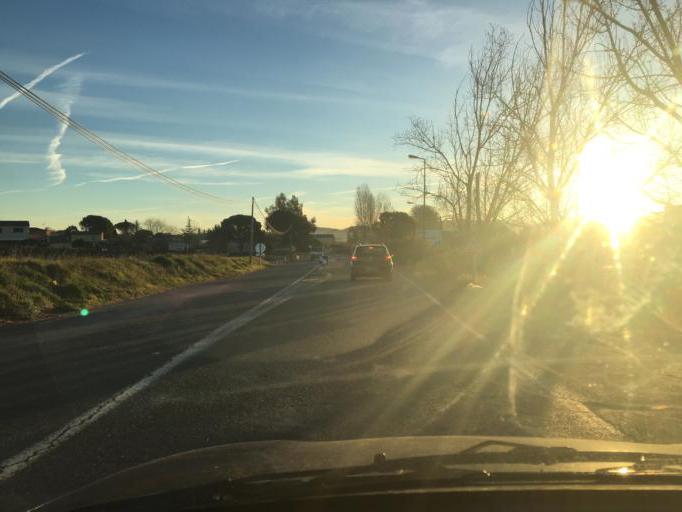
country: FR
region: Provence-Alpes-Cote d'Azur
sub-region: Departement du Var
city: Les Arcs
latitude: 43.4491
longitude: 6.4725
